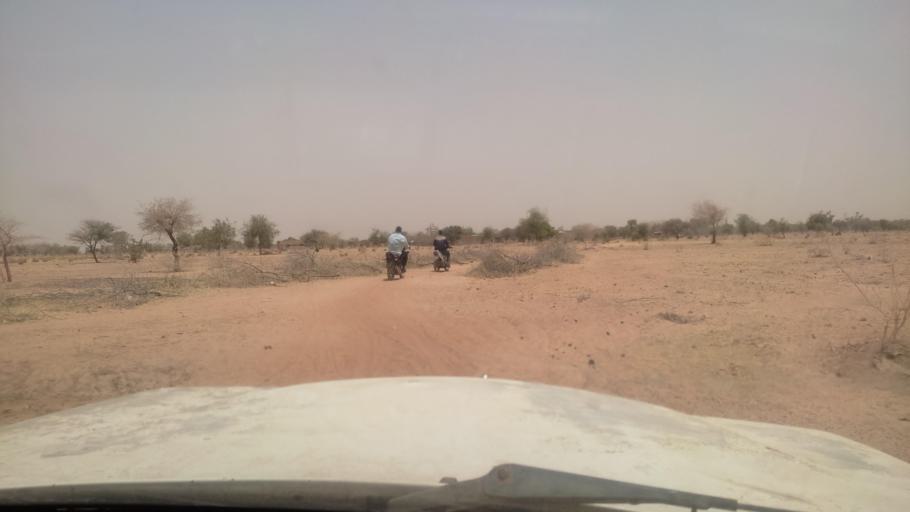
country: BF
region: Est
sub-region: Gnagna Province
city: Bogande
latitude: 13.0026
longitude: -0.0948
